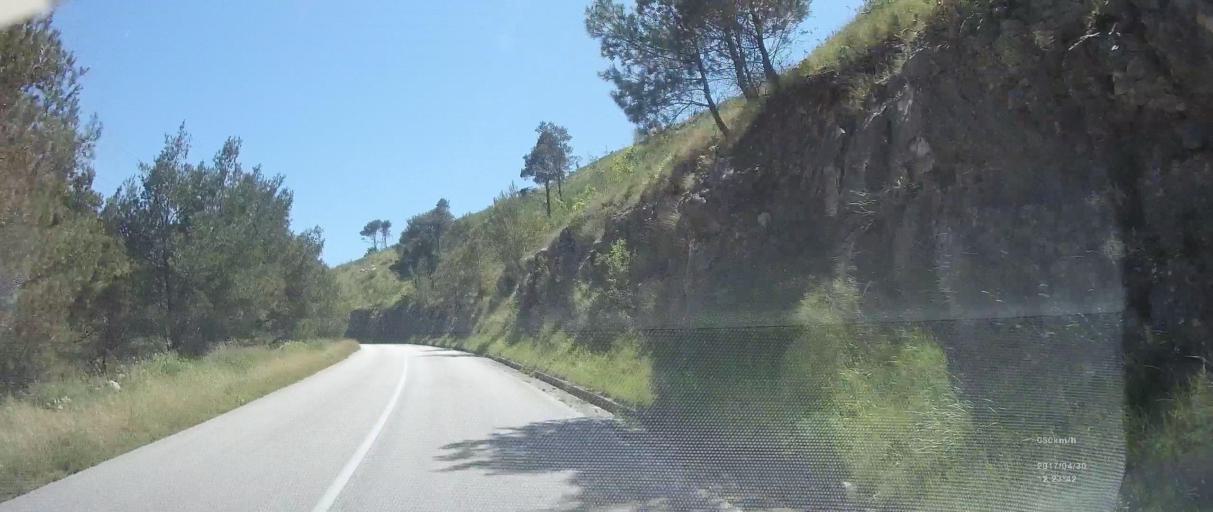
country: HR
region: Splitsko-Dalmatinska
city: Zrnovnica
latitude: 43.5148
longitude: 16.5798
